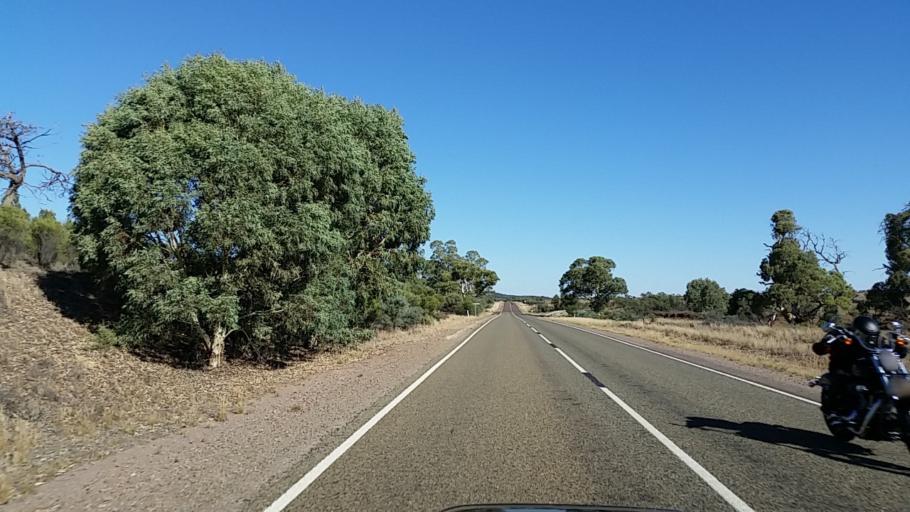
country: AU
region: South Australia
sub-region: Flinders Ranges
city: Quorn
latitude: -32.4764
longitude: 138.5415
